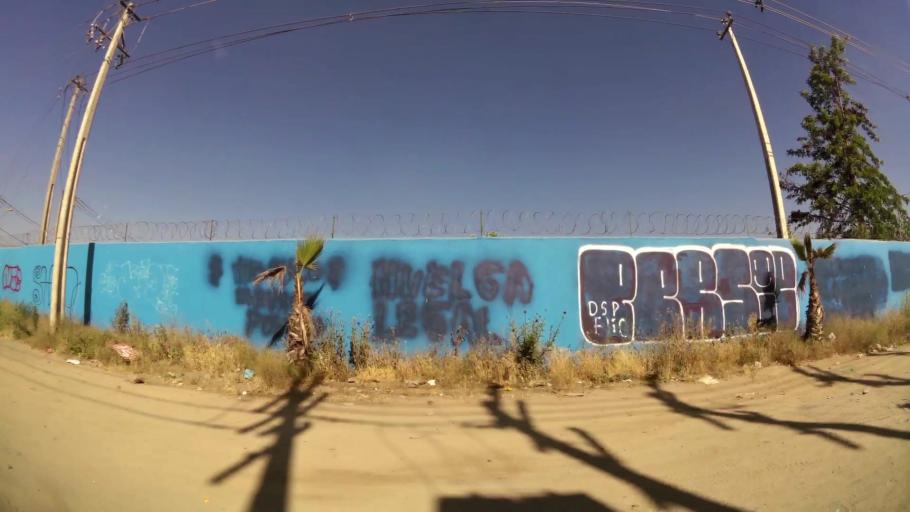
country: CL
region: Santiago Metropolitan
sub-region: Provincia de Maipo
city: San Bernardo
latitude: -33.5559
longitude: -70.6930
